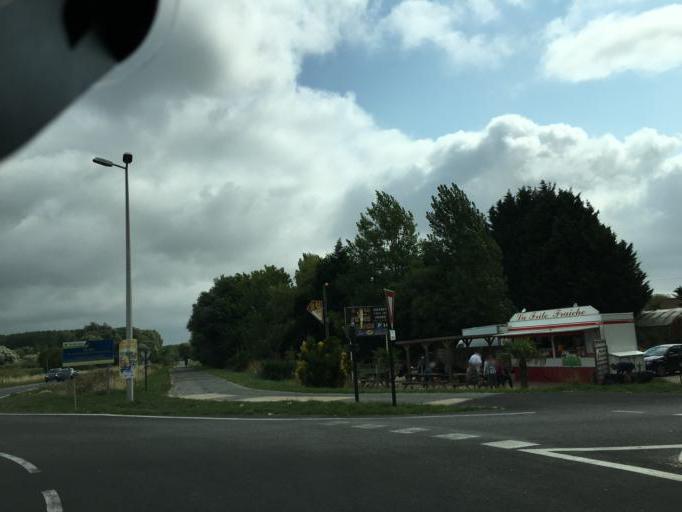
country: FR
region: Nord-Pas-de-Calais
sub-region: Departement du Pas-de-Calais
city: Rang-du-Fliers
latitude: 50.4069
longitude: 1.6334
